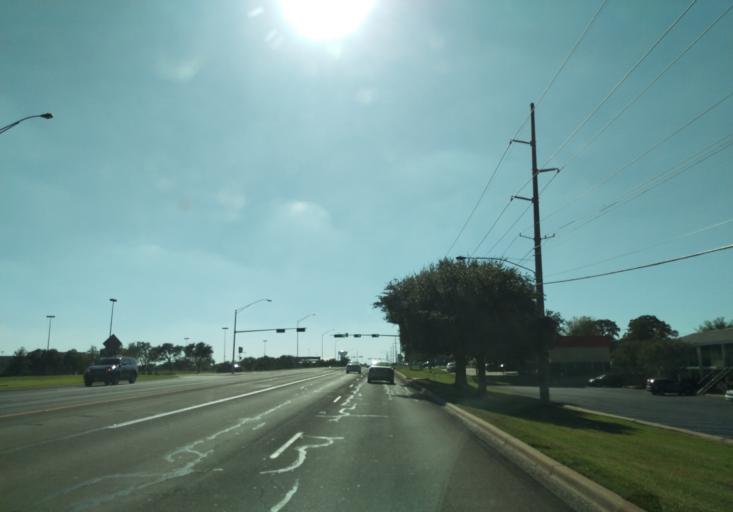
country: US
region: Texas
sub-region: Brazos County
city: College Station
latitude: 30.6284
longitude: -96.3040
